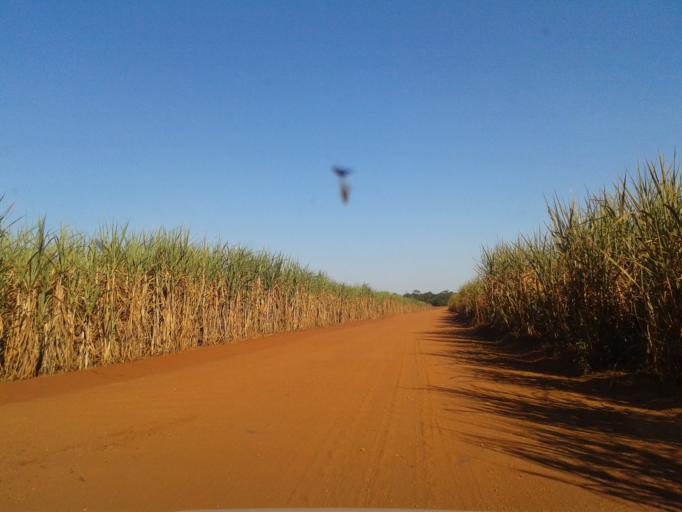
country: BR
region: Minas Gerais
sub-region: Santa Vitoria
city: Santa Vitoria
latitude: -18.8800
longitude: -50.0476
